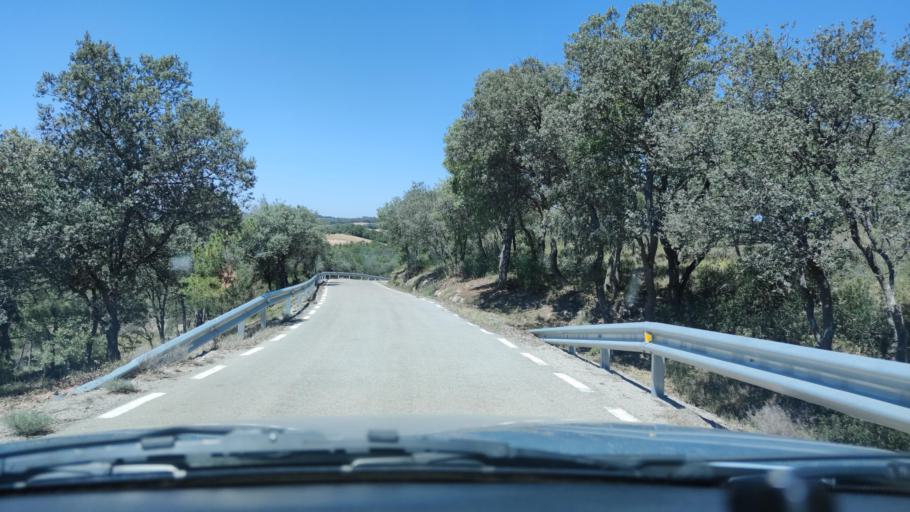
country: ES
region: Catalonia
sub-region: Provincia de Lleida
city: Tora de Riubregos
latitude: 41.8545
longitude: 1.4317
